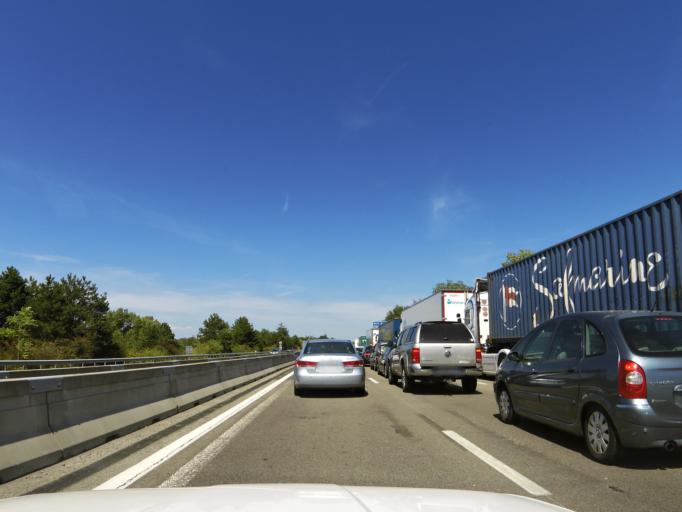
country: FR
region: Rhone-Alpes
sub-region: Departement de l'Ardeche
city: Cruas
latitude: 44.6393
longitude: 4.7918
